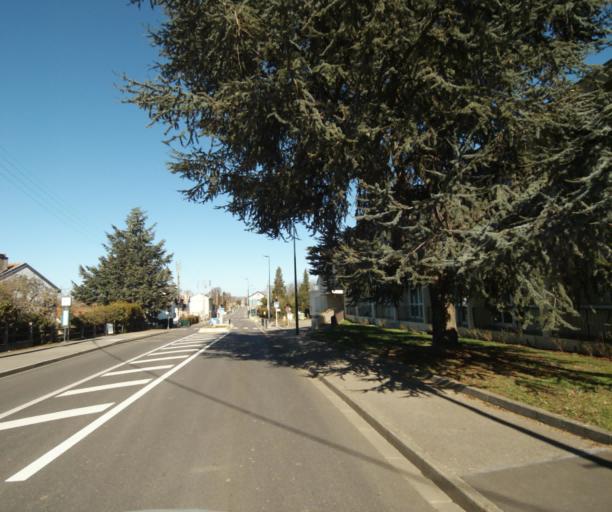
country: FR
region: Lorraine
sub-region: Departement de Meurthe-et-Moselle
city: Heillecourt
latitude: 48.6588
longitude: 6.2065
